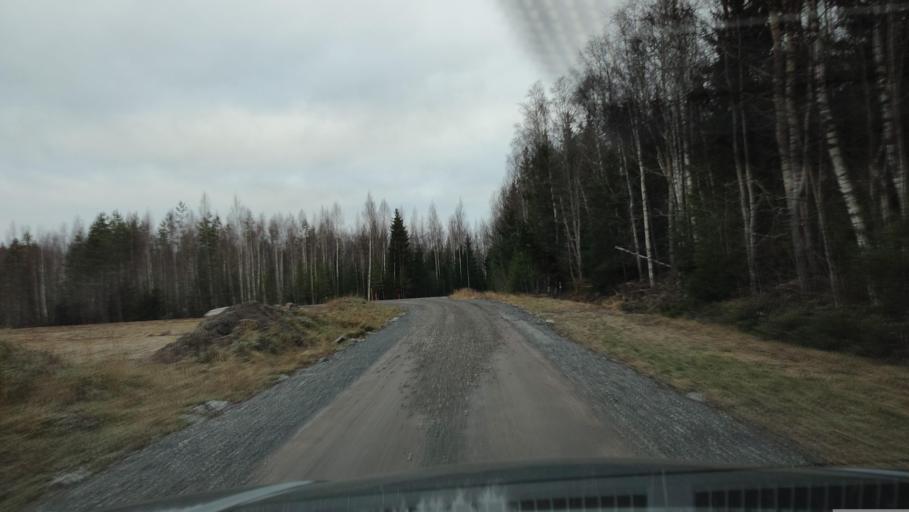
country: FI
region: Southern Ostrobothnia
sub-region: Suupohja
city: Karijoki
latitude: 62.2183
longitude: 21.6010
